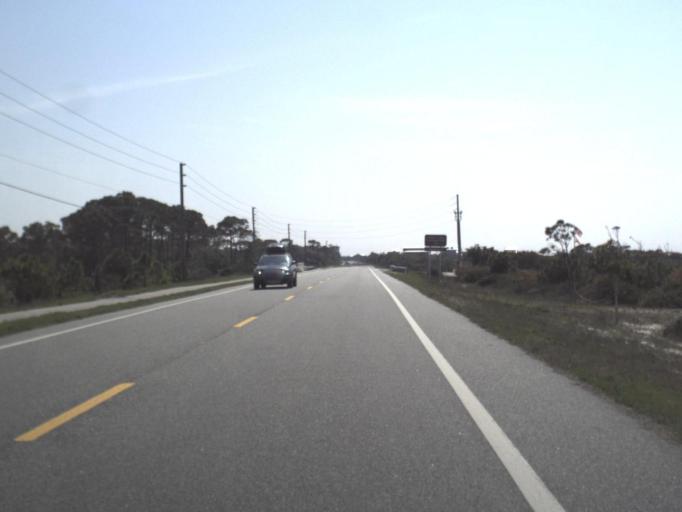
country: US
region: Florida
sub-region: Gulf County
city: Port Saint Joe
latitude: 29.7289
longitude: -85.3901
